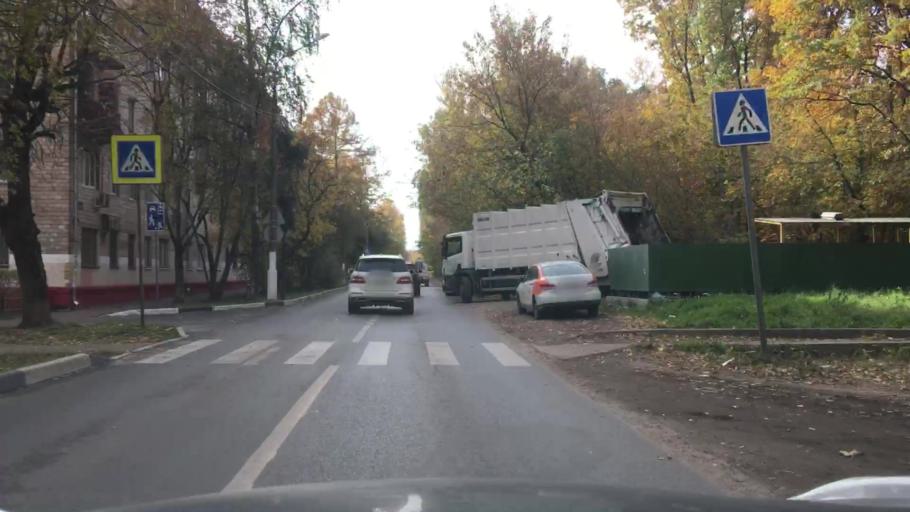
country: RU
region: Moskovskaya
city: Balashikha
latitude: 55.8018
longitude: 37.9272
